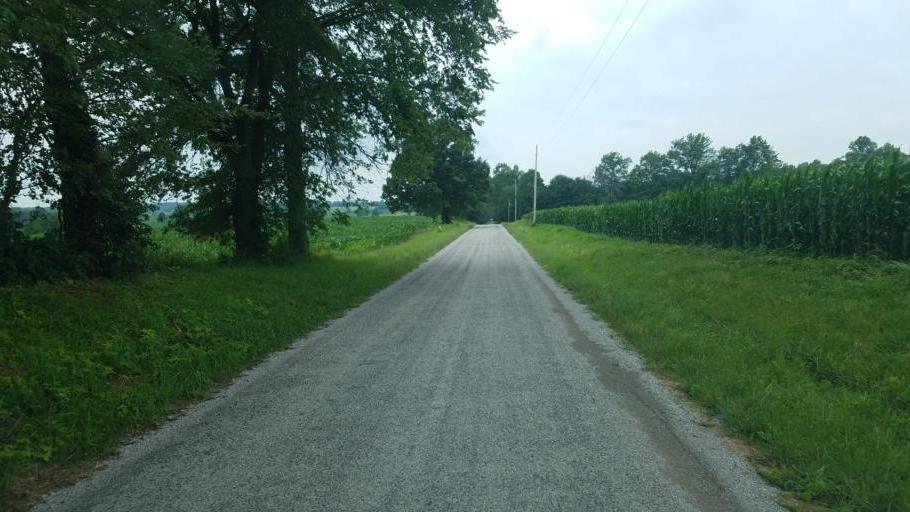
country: US
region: Ohio
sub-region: Licking County
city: Utica
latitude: 40.1975
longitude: -82.5208
